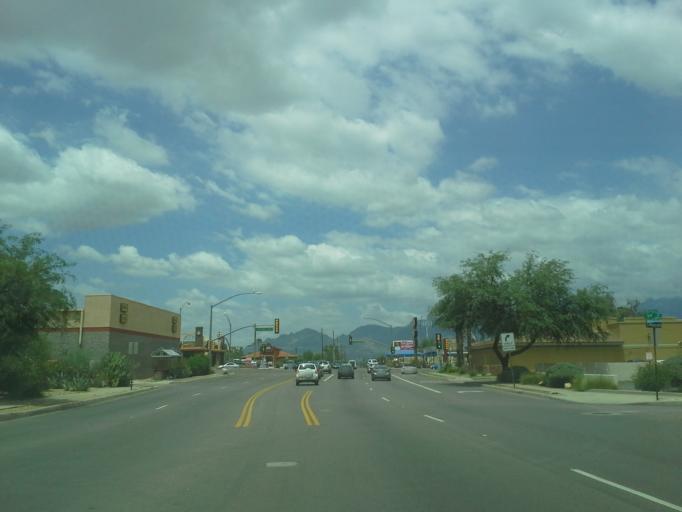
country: US
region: Arizona
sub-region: Pima County
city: Tucson
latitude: 32.2349
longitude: -110.9268
